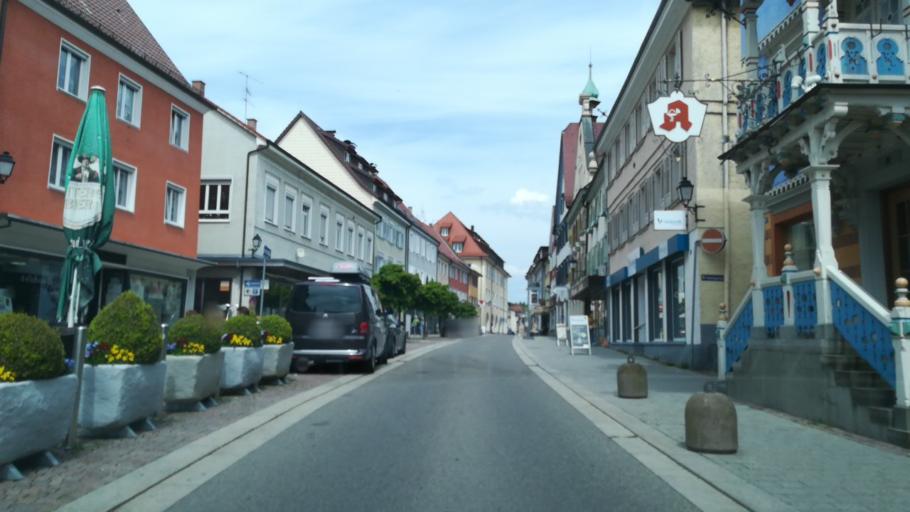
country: DE
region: Baden-Wuerttemberg
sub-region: Freiburg Region
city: Stockach
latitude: 47.8521
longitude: 9.0121
